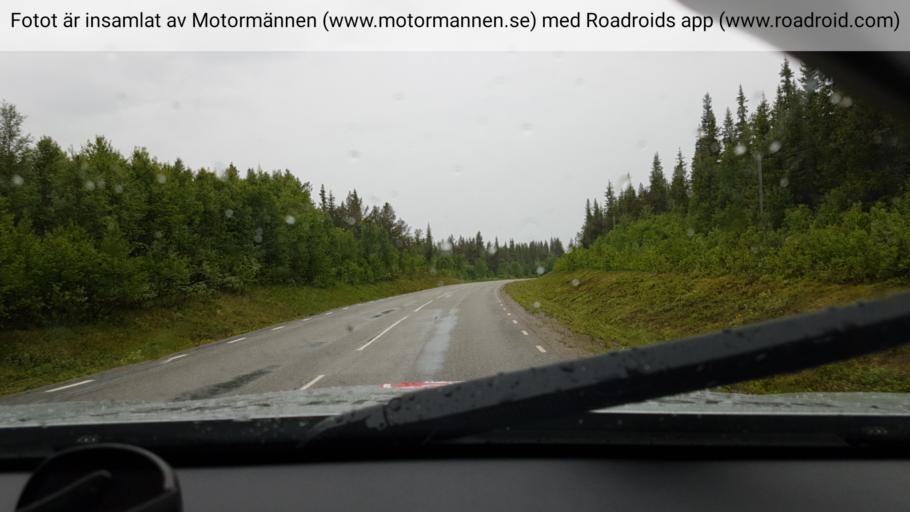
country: SE
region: Vaesterbotten
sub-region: Storumans Kommun
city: Fristad
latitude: 65.8718
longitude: 16.4140
